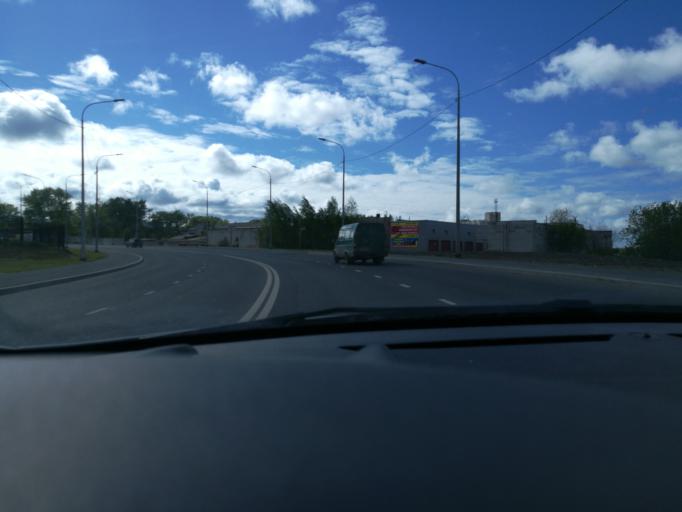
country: RU
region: Arkhangelskaya
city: Arkhangel'sk
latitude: 64.5658
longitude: 40.5478
